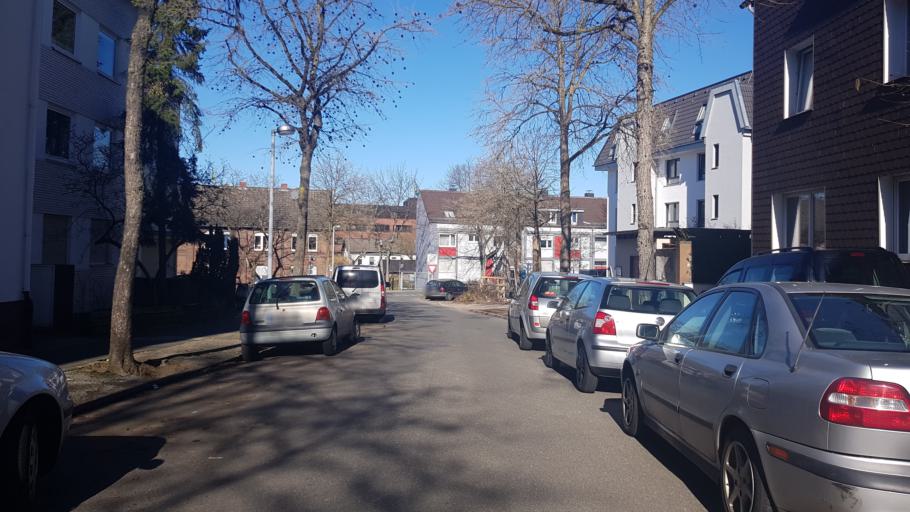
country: DE
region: North Rhine-Westphalia
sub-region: Regierungsbezirk Dusseldorf
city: Muelheim (Ruhr)
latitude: 51.4214
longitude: 6.8525
